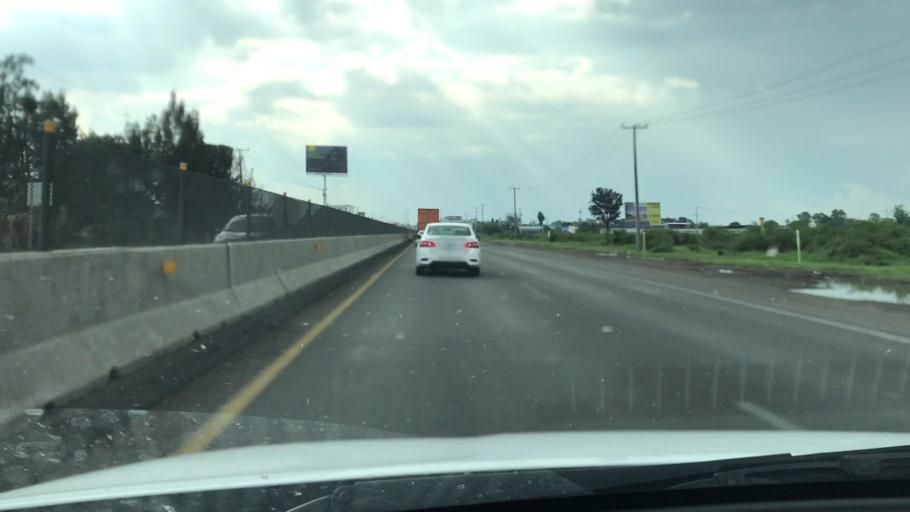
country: MX
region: Guanajuato
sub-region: Irapuato
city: Cuarta Brigada
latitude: 20.6307
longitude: -101.2737
